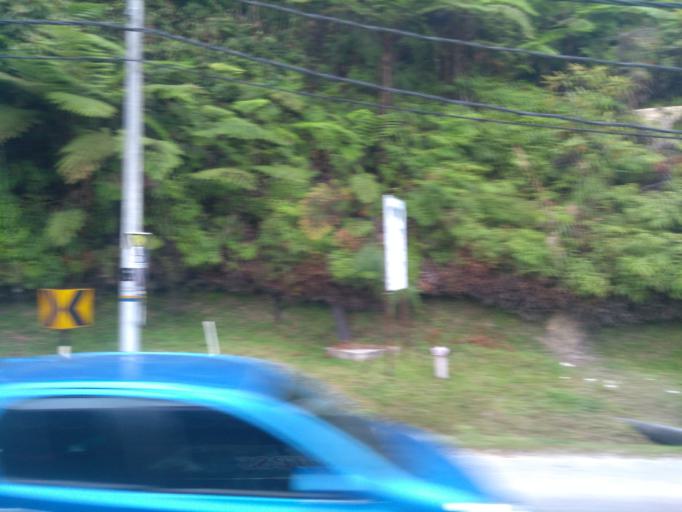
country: MY
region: Pahang
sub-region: Cameron Highlands
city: Tanah Rata
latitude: 4.5064
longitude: 101.4066
